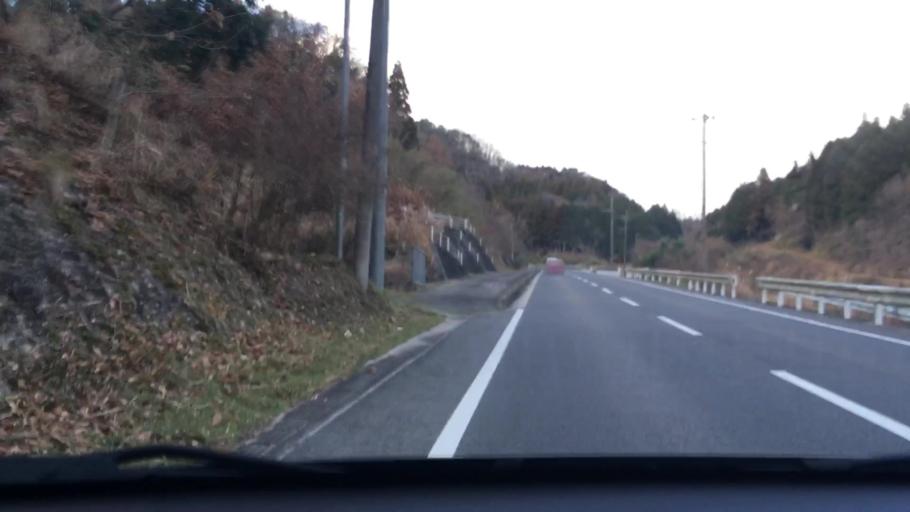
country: JP
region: Oita
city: Bungo-Takada-shi
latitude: 33.4714
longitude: 131.3846
